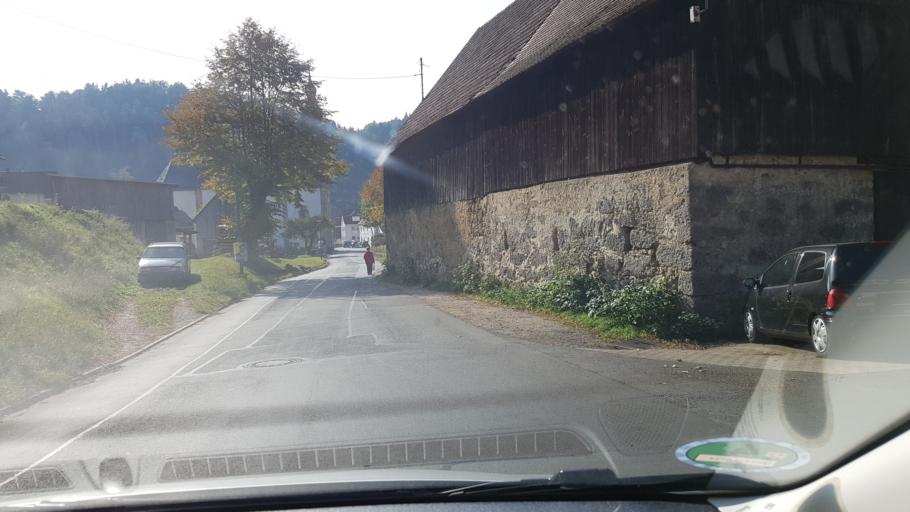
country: DE
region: Bavaria
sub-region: Upper Franconia
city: Waischenfeld
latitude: 49.8142
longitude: 11.3533
